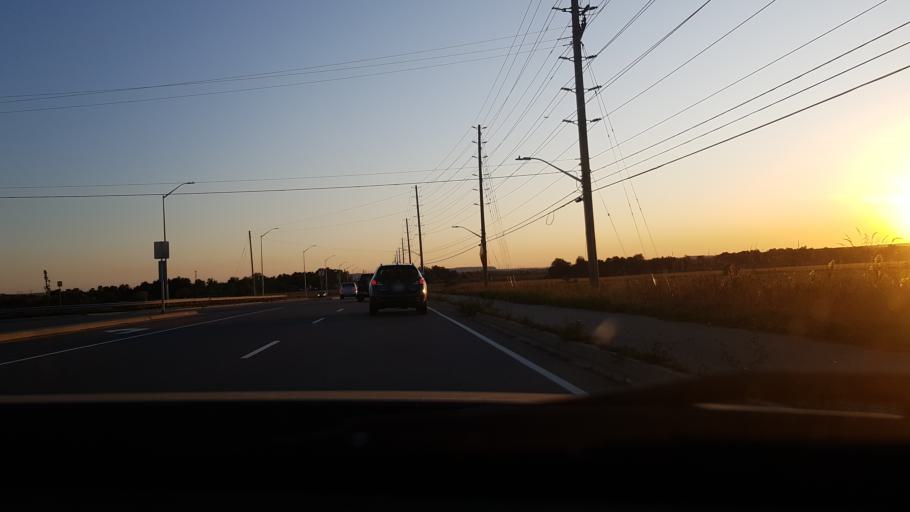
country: CA
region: Ontario
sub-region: Halton
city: Milton
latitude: 43.5847
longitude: -79.8237
